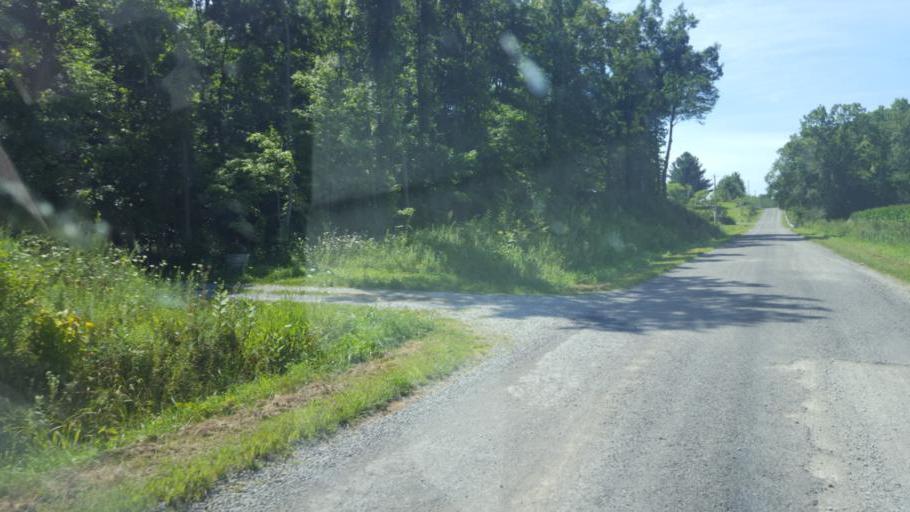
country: US
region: Ohio
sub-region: Morrow County
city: Mount Gilead
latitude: 40.4632
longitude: -82.7241
